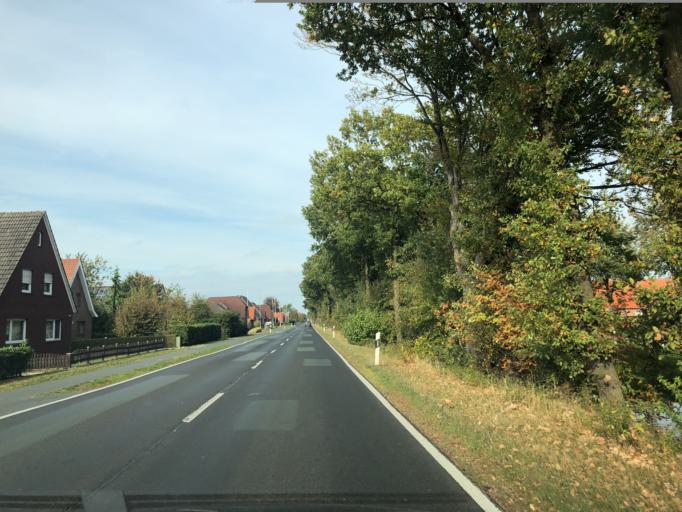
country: DE
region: Lower Saxony
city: Surwold
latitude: 53.0321
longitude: 7.4737
